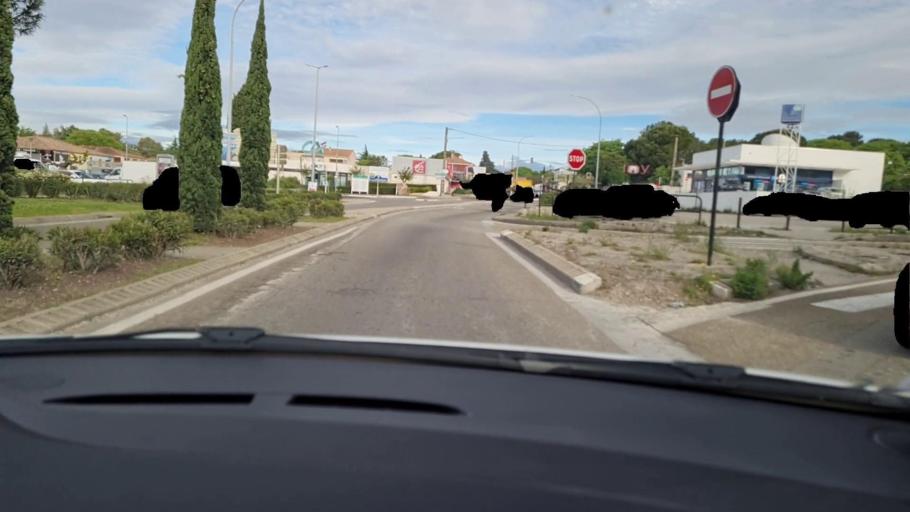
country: FR
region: Languedoc-Roussillon
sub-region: Departement du Gard
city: Nimes
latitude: 43.8402
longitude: 4.3191
